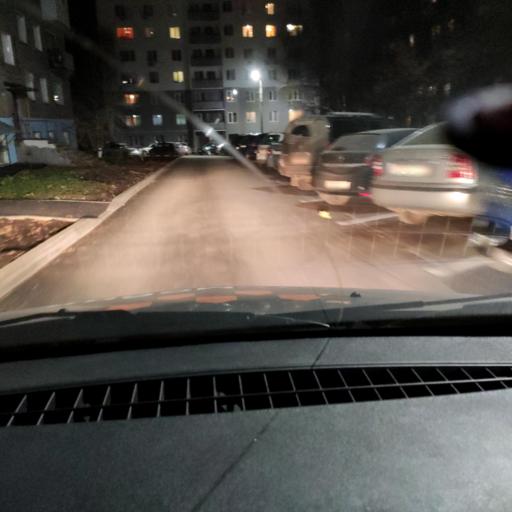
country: RU
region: Bashkortostan
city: Ufa
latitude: 54.7634
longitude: 55.9944
